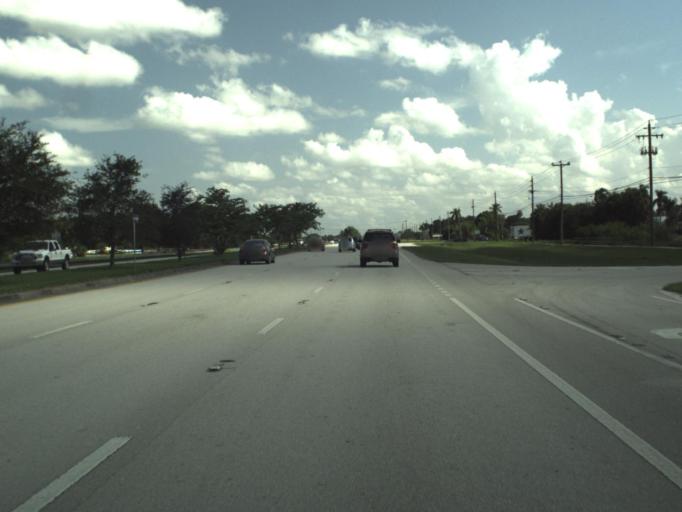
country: US
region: Florida
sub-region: Palm Beach County
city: Greenacres City
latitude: 26.5563
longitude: -80.2059
